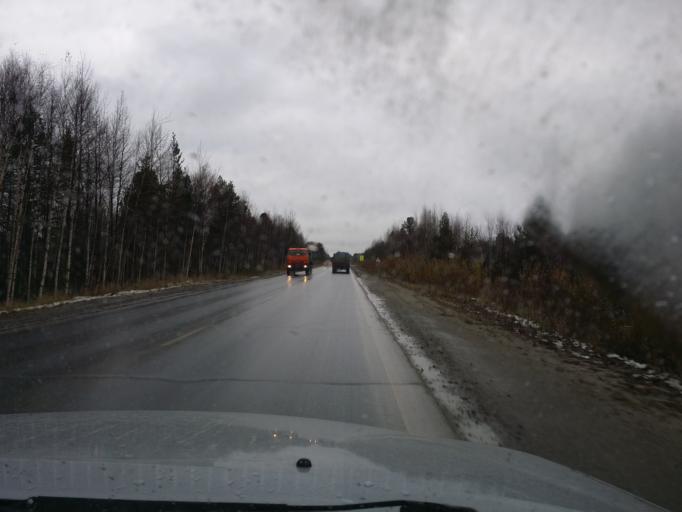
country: RU
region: Khanty-Mansiyskiy Avtonomnyy Okrug
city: Megion
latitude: 61.1452
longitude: 75.7551
